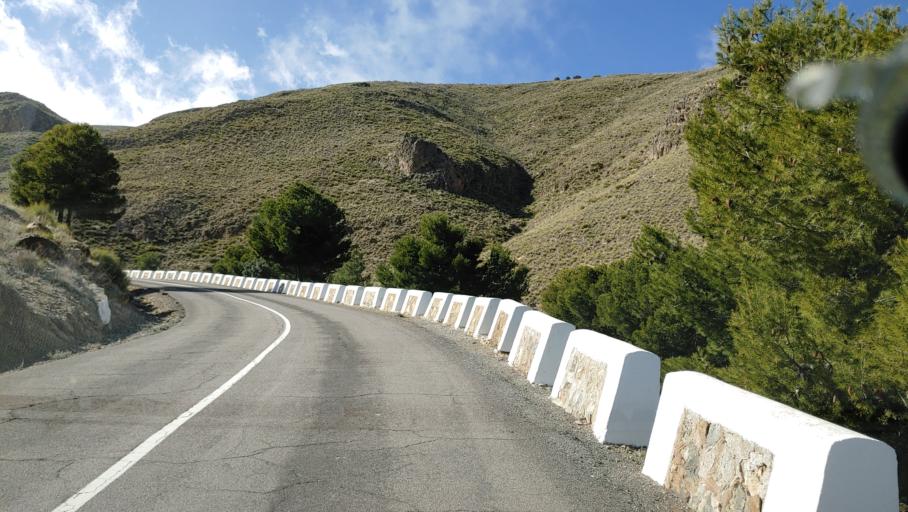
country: ES
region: Andalusia
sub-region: Provincia de Almeria
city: Enix
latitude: 36.9184
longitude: -2.5997
